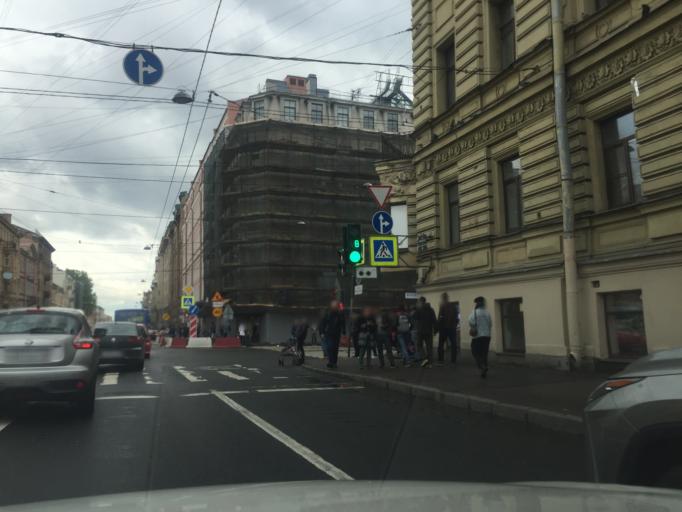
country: RU
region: St.-Petersburg
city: Vasyl'evsky Ostrov
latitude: 59.9427
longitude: 30.2756
